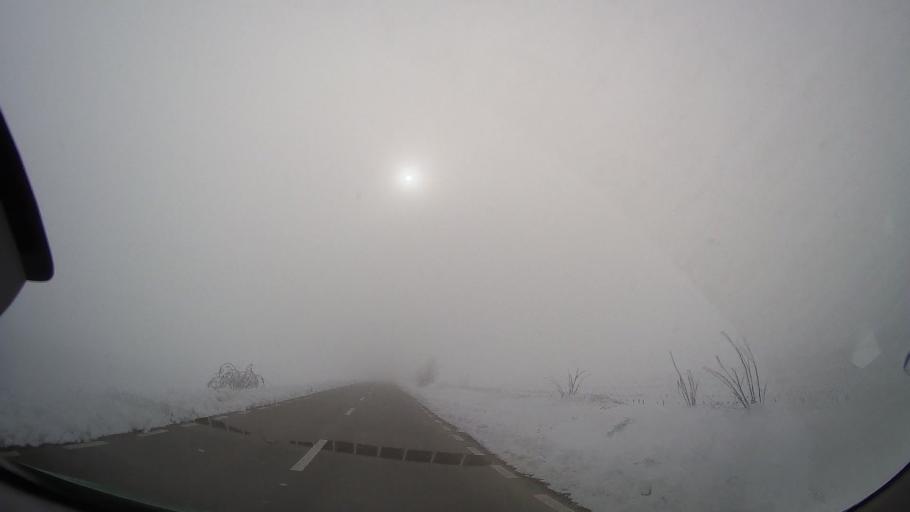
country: RO
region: Iasi
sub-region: Comuna Valea Seaca
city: Valea Seaca
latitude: 47.2793
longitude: 26.6706
